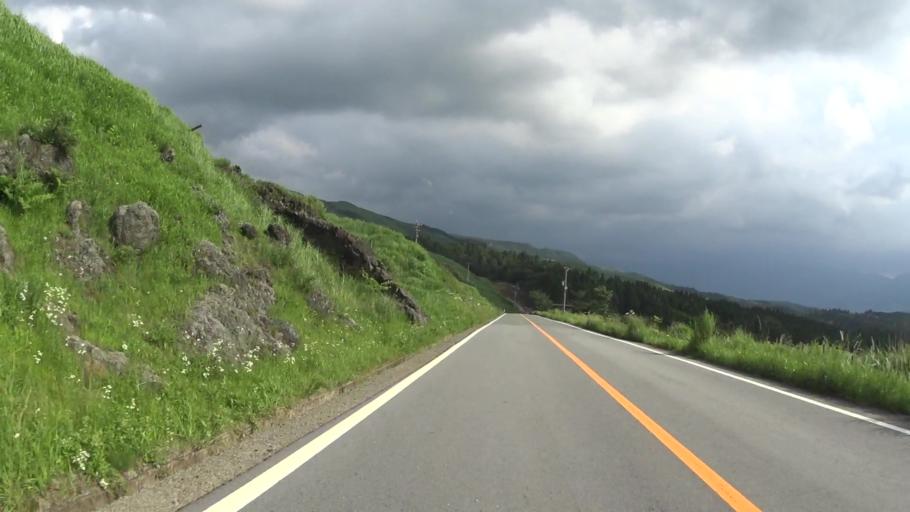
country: JP
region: Kumamoto
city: Aso
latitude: 32.9022
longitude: 131.0297
